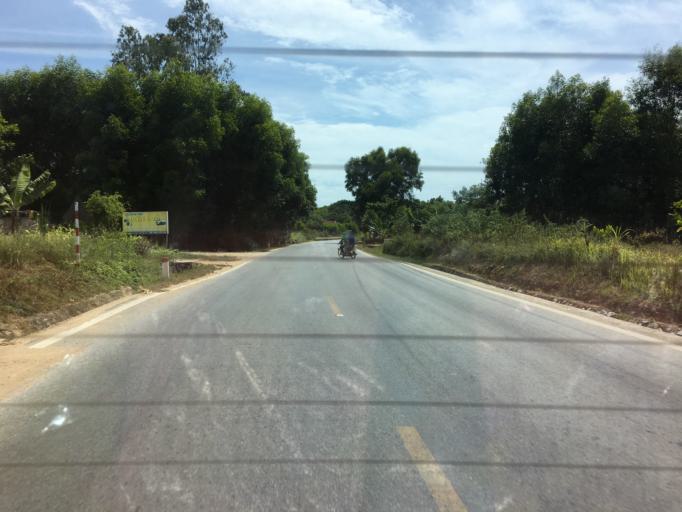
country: VN
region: Nghe An
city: Cau Giat
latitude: 19.2031
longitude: 105.4354
